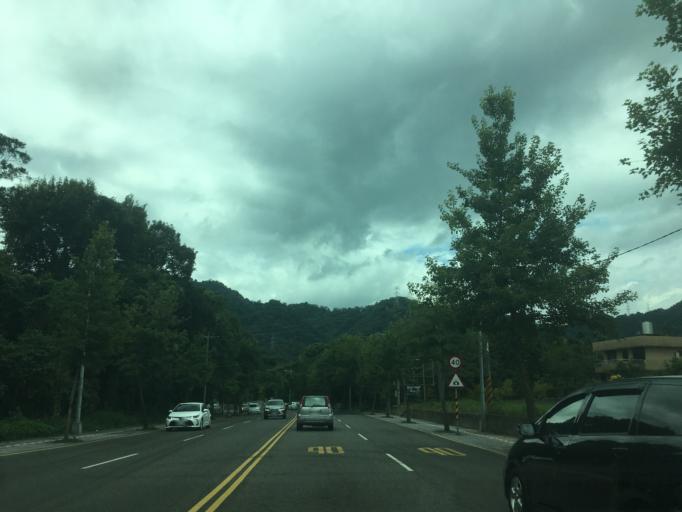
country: TW
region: Taiwan
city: Daxi
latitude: 24.8444
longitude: 121.2860
